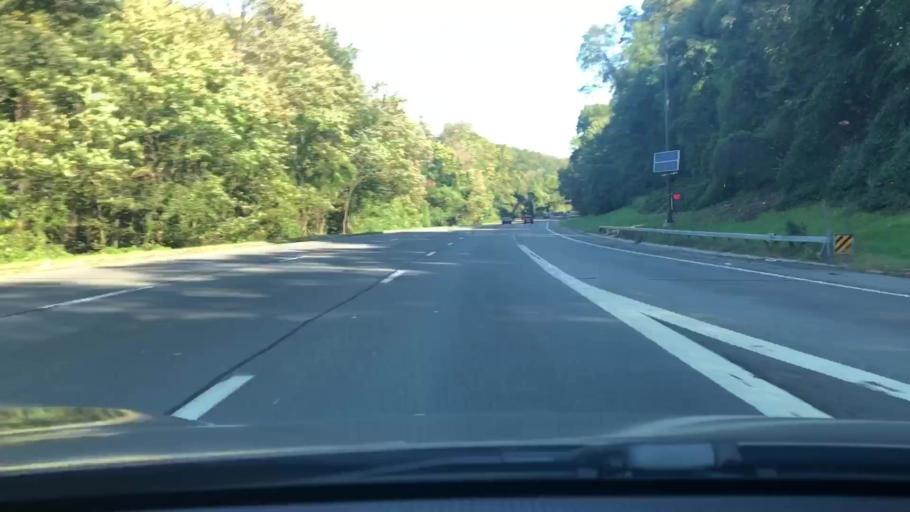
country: US
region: New York
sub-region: Westchester County
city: Greenville
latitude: 40.9905
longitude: -73.8385
